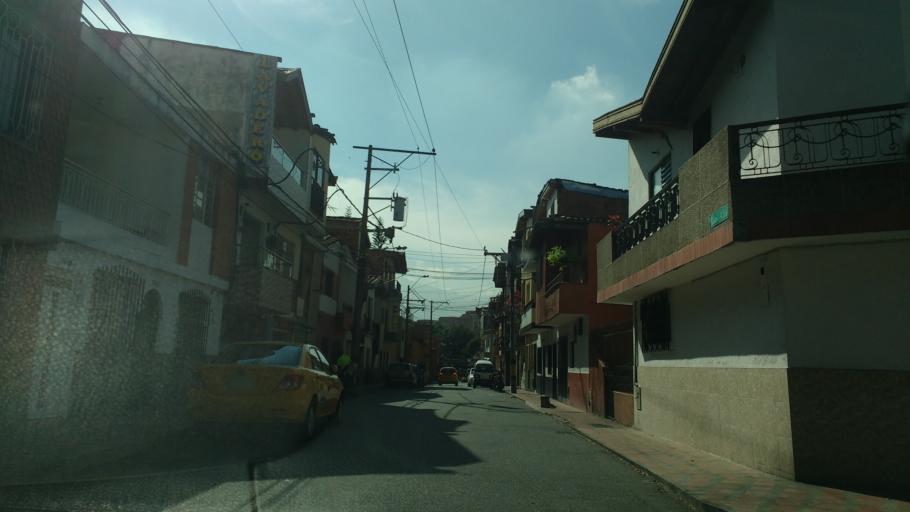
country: CO
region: Antioquia
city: Medellin
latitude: 6.2524
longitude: -75.5962
